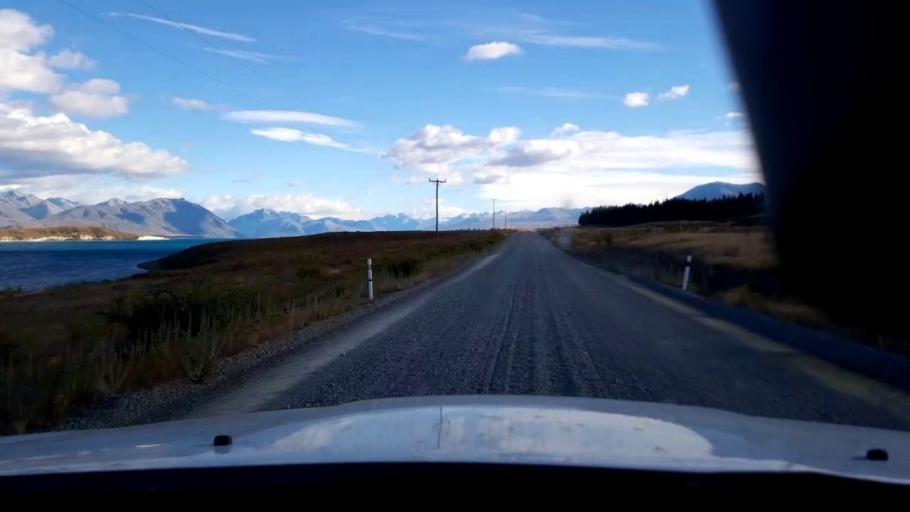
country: NZ
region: Canterbury
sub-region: Timaru District
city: Pleasant Point
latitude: -43.9895
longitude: 170.5033
